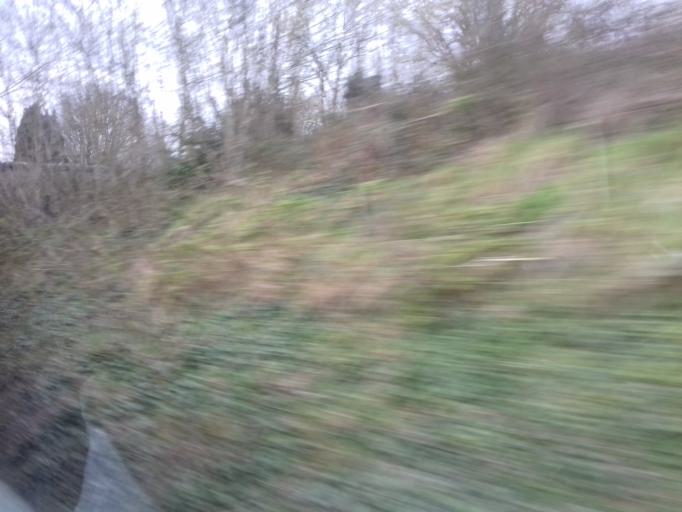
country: IE
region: Leinster
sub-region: An Iarmhi
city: An Muileann gCearr
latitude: 53.6014
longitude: -7.3971
